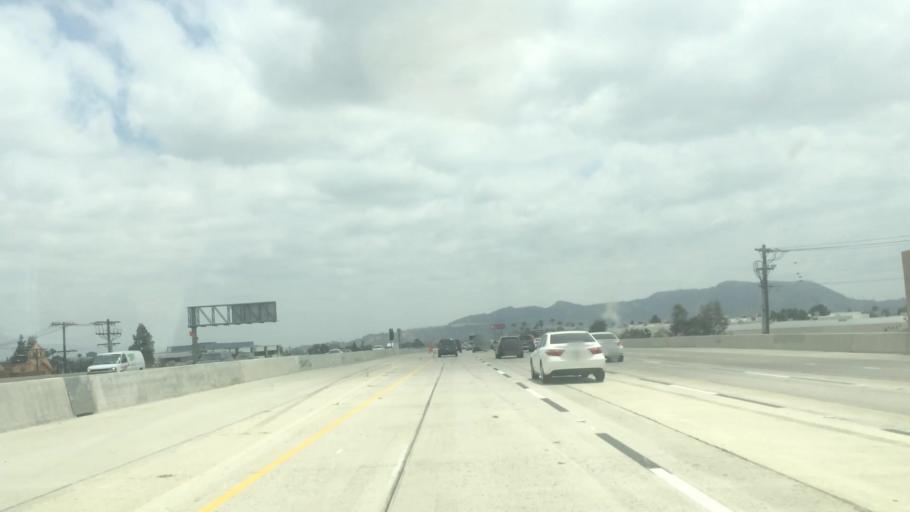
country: US
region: California
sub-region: Los Angeles County
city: Burbank
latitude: 34.2072
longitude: -118.3437
